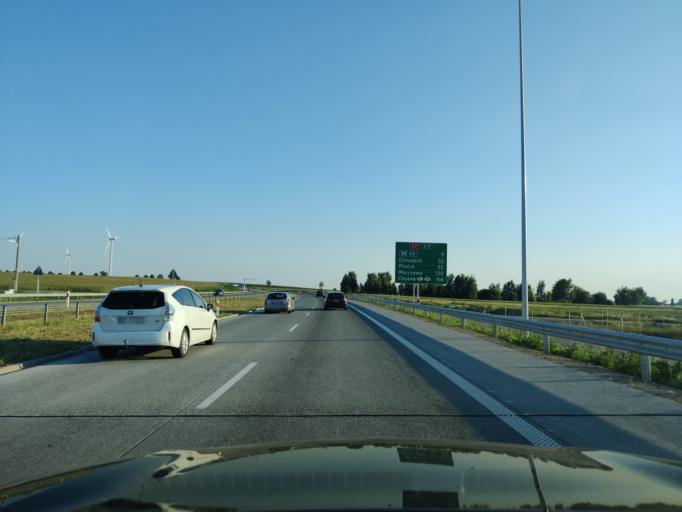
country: PL
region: Masovian Voivodeship
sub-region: Powiat mlawski
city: Wisniewo
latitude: 53.0685
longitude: 20.3700
